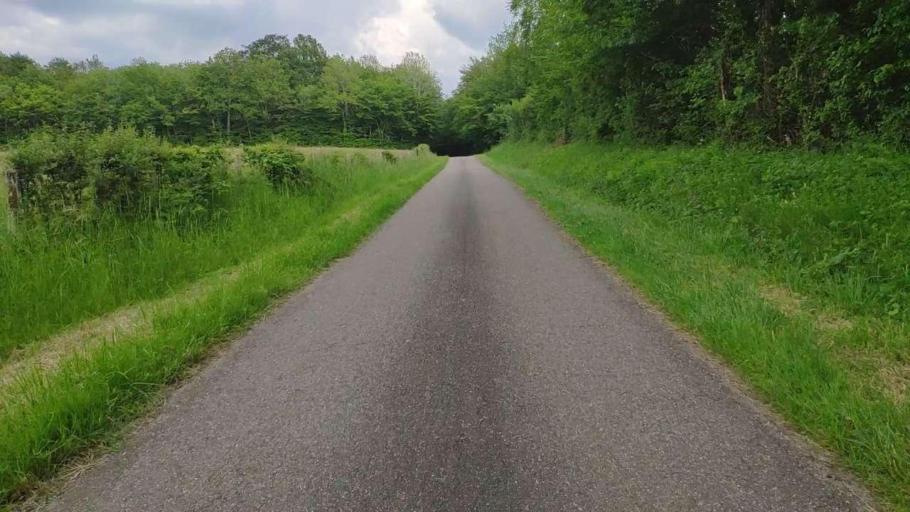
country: FR
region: Bourgogne
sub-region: Departement de Saone-et-Loire
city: Saint-Germain-du-Bois
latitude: 46.7964
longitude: 5.3507
